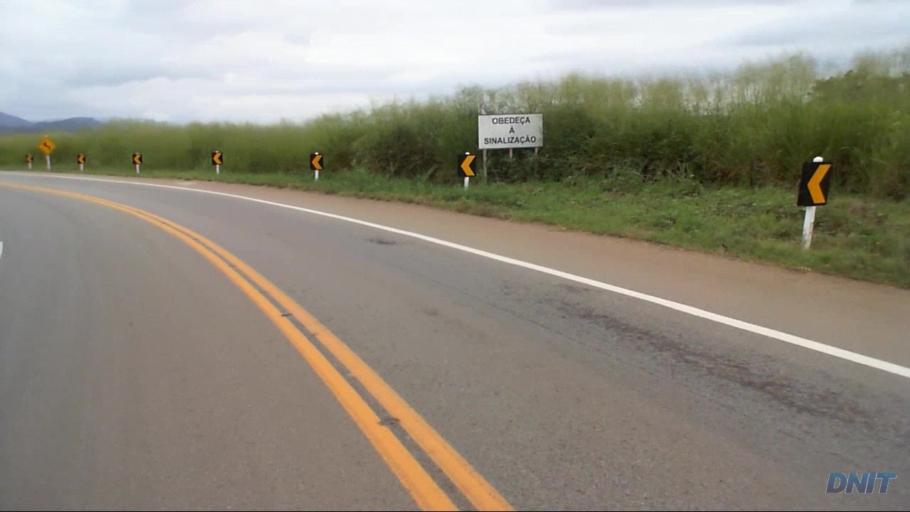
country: BR
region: Minas Gerais
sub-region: Nova Era
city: Nova Era
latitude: -19.7962
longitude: -43.0531
